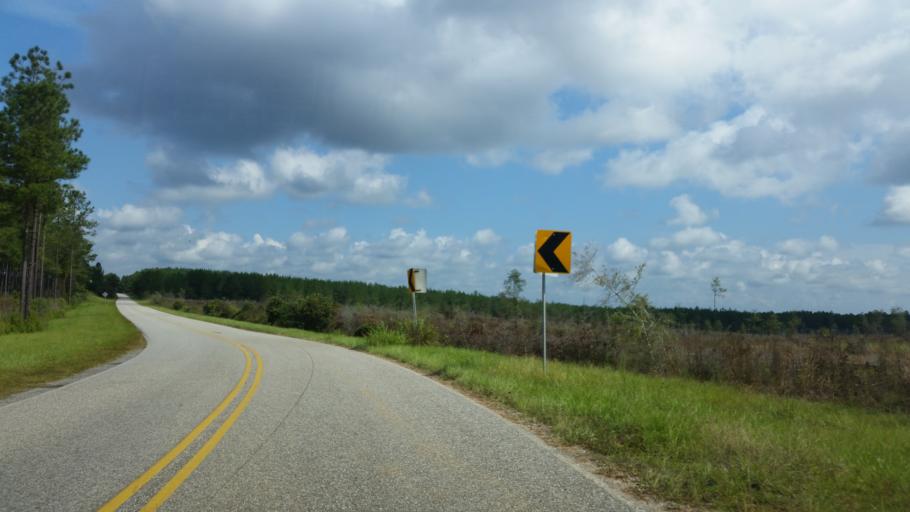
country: US
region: Florida
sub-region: Escambia County
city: Cantonment
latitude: 30.6735
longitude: -87.4705
